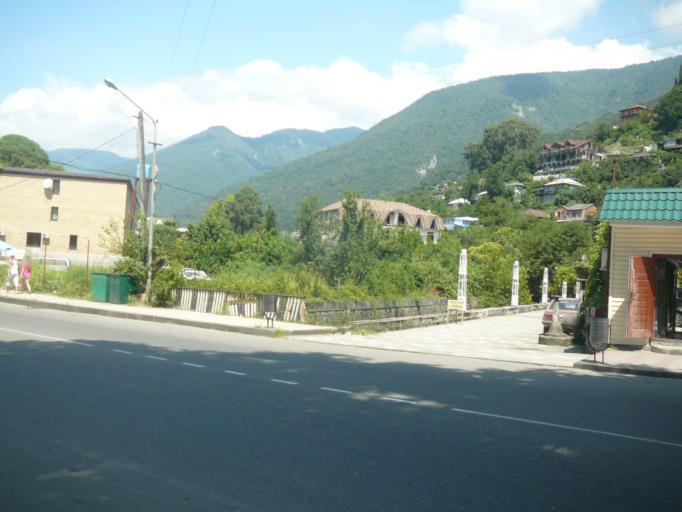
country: GE
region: Abkhazia
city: Gagra
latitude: 43.2938
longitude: 40.2597
